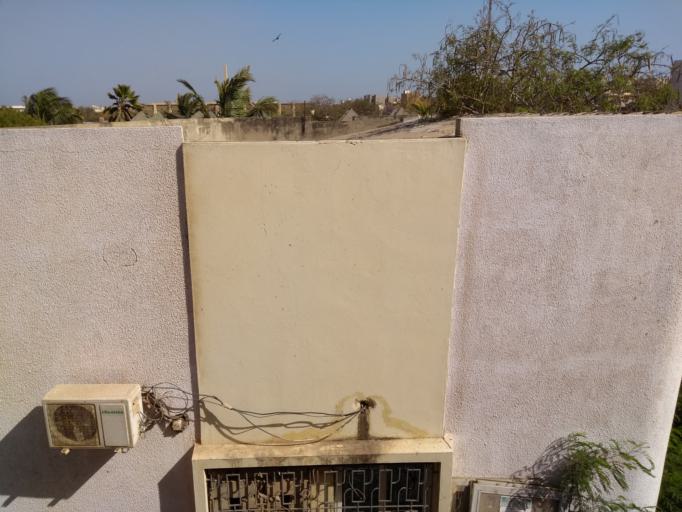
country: SN
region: Dakar
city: Dakar
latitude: 14.6984
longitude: -17.4510
